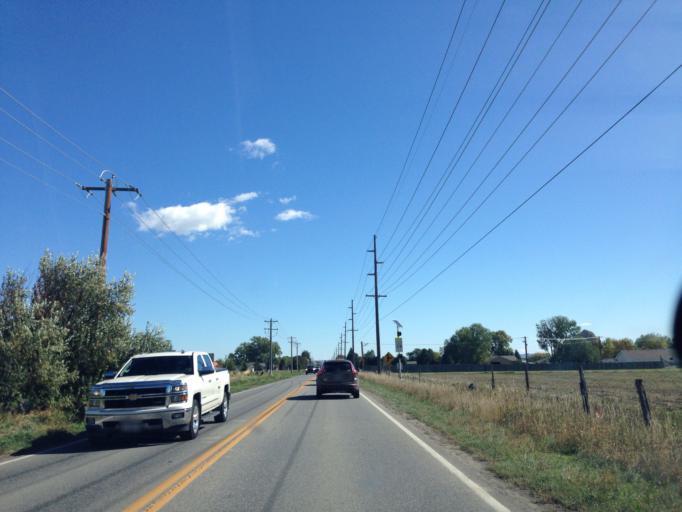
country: US
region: Montana
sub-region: Yellowstone County
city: Billings
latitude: 45.7841
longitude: -108.6419
